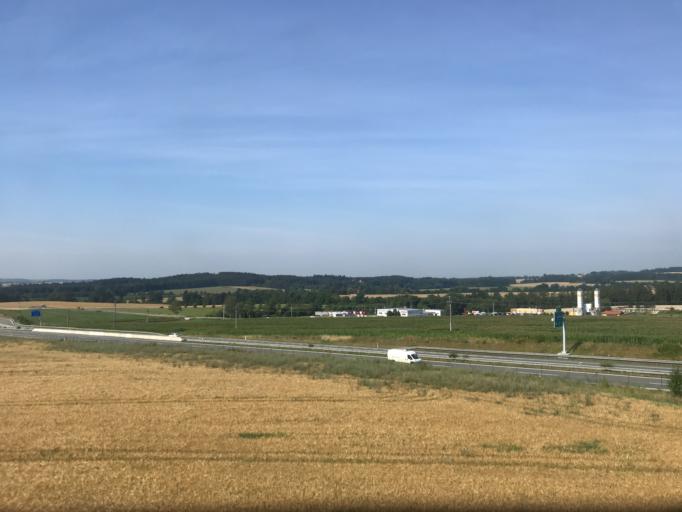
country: CZ
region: Jihocesky
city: Chotoviny
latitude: 49.4781
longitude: 14.6619
